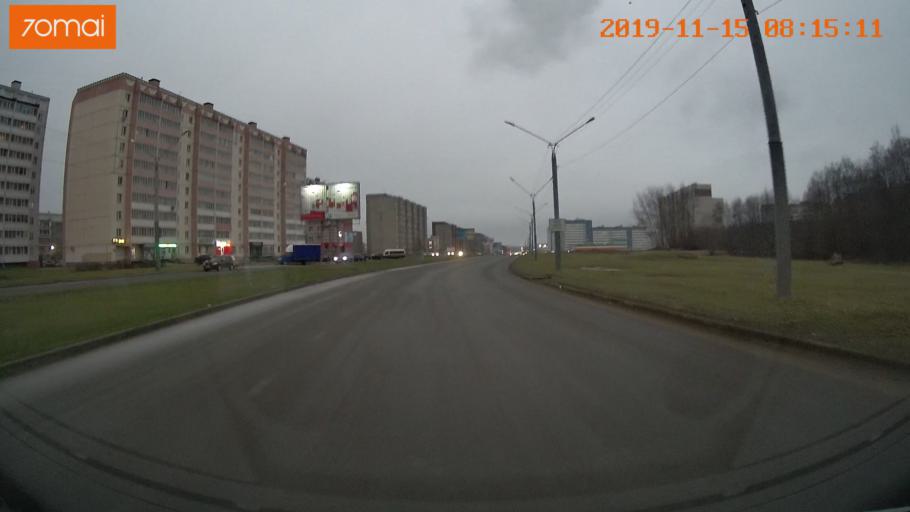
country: RU
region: Vologda
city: Cherepovets
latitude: 59.0805
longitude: 37.9237
